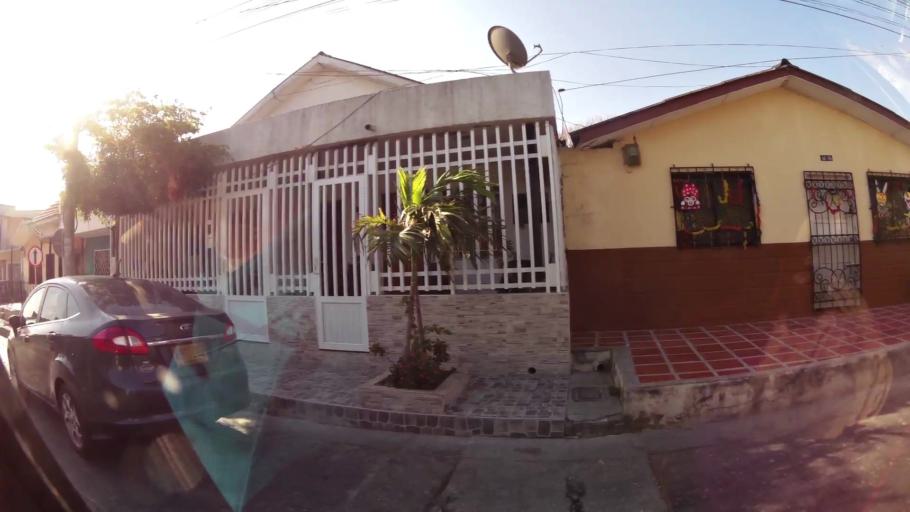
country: CO
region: Atlantico
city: Barranquilla
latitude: 10.9917
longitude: -74.7867
